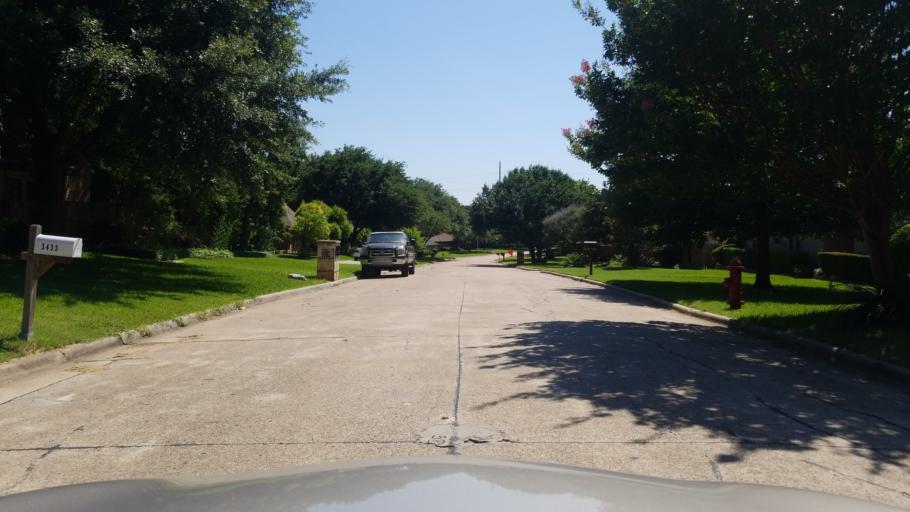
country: US
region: Texas
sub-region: Dallas County
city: Grand Prairie
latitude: 32.6899
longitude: -96.9947
